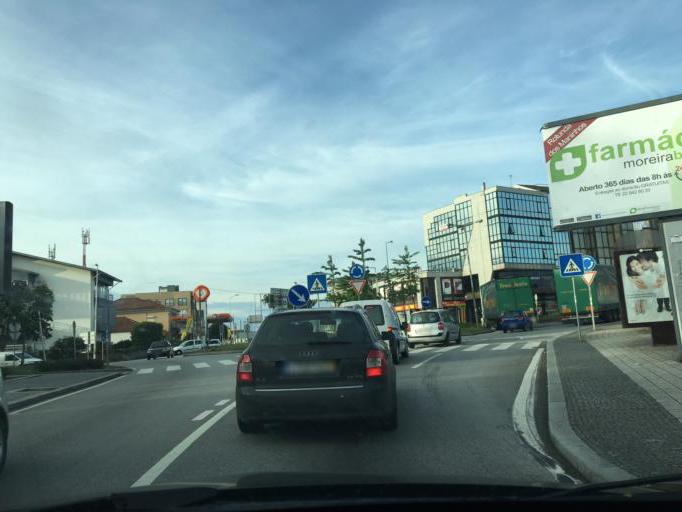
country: PT
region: Porto
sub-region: Maia
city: Anta
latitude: 41.2606
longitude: -8.6162
